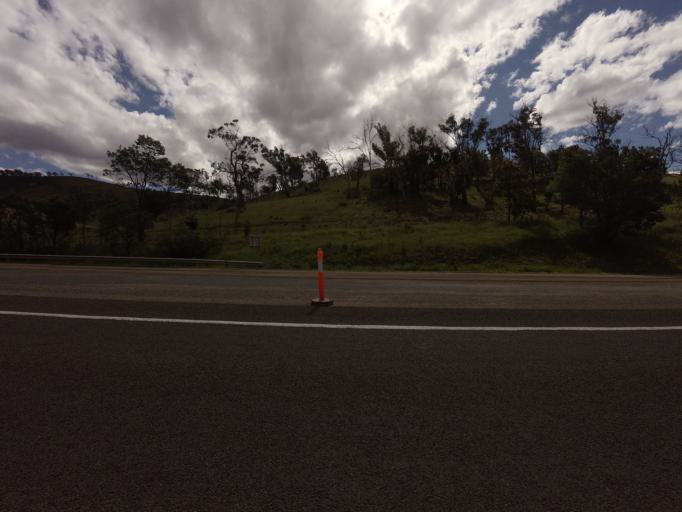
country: AU
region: Tasmania
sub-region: Brighton
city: Bridgewater
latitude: -42.2225
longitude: 147.4102
